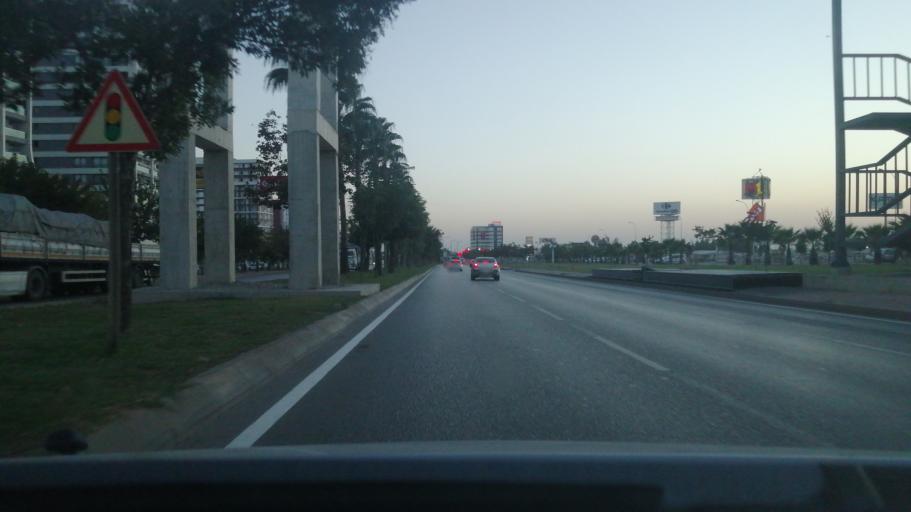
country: TR
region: Adana
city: Seyhan
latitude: 37.0189
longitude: 35.2521
